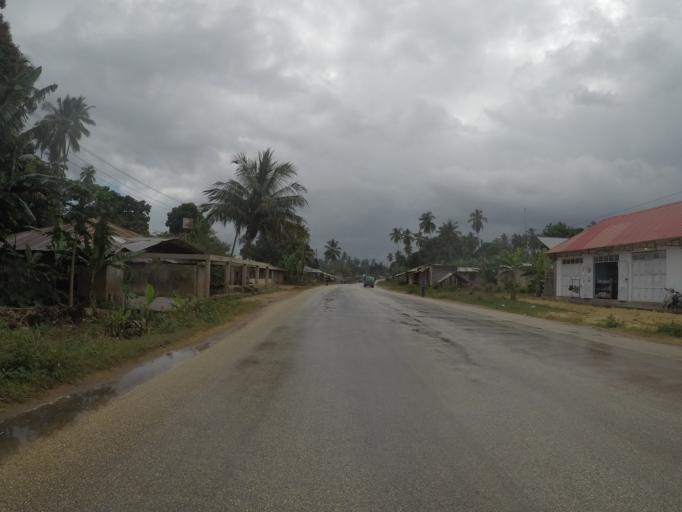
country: TZ
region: Zanzibar Central/South
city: Koani
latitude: -6.0472
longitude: 39.2270
